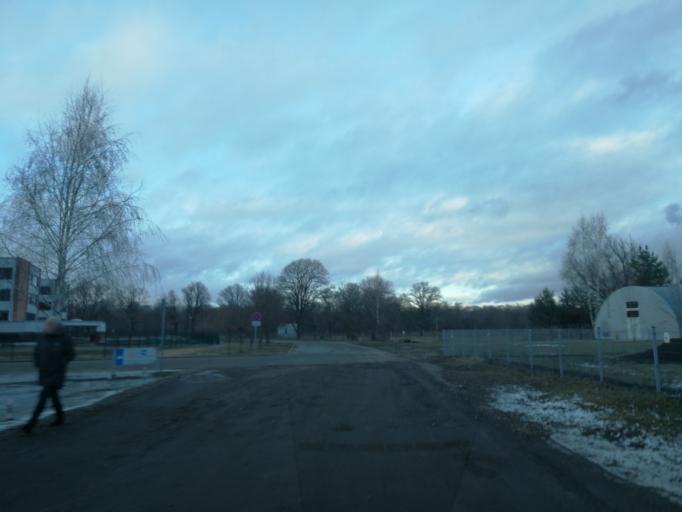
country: LV
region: Adazi
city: Adazi
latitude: 57.0777
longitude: 24.3406
